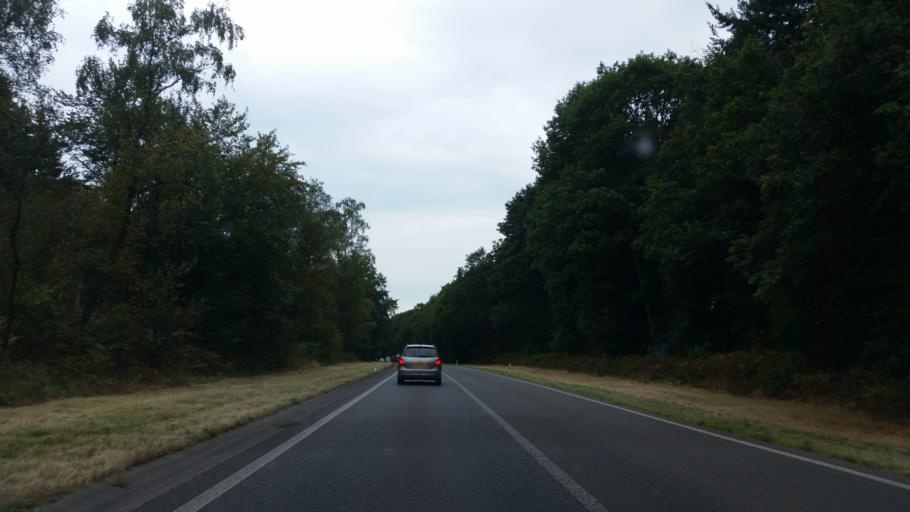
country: NL
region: Gelderland
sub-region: Gemeente Ede
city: Ede
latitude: 52.0648
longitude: 5.6883
